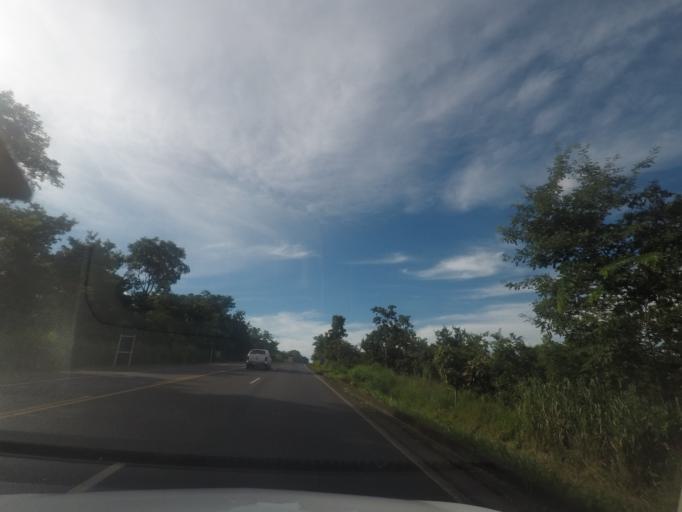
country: BR
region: Minas Gerais
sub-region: Monte Alegre De Minas
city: Monte Alegre de Minas
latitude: -18.9377
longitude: -49.0285
